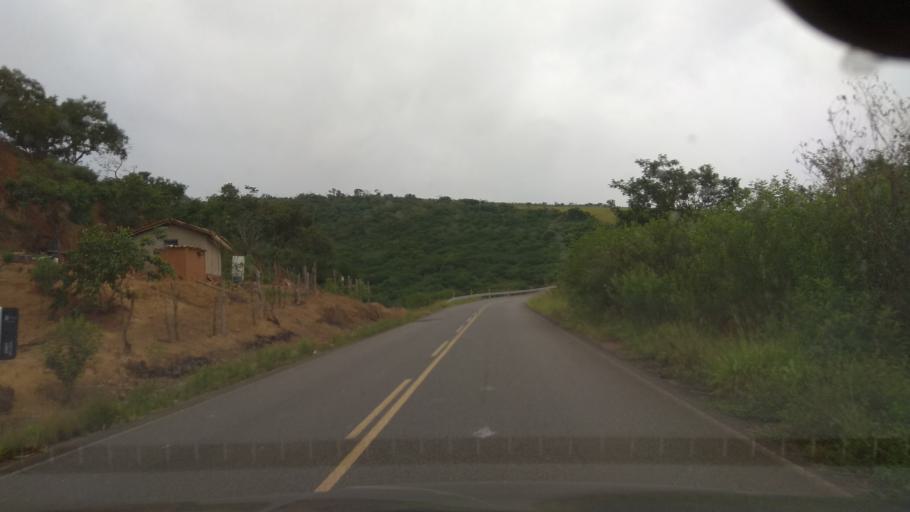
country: BR
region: Bahia
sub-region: Santa Ines
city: Santa Ines
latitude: -13.2392
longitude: -39.7519
